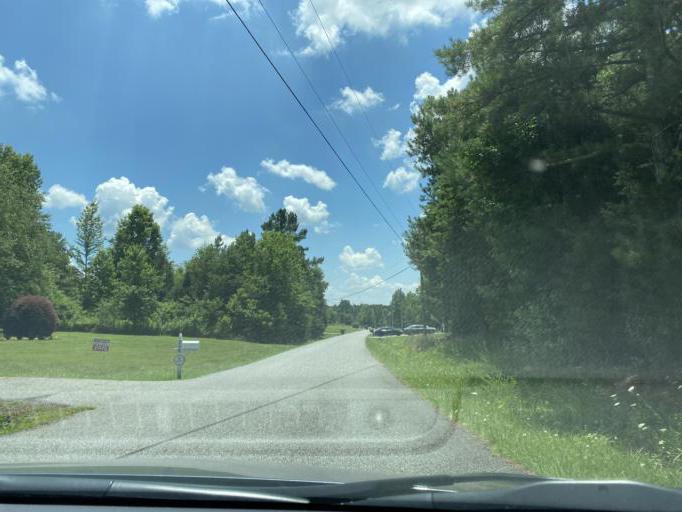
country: US
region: South Carolina
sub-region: Cherokee County
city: Gaffney
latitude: 35.1286
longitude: -81.7188
